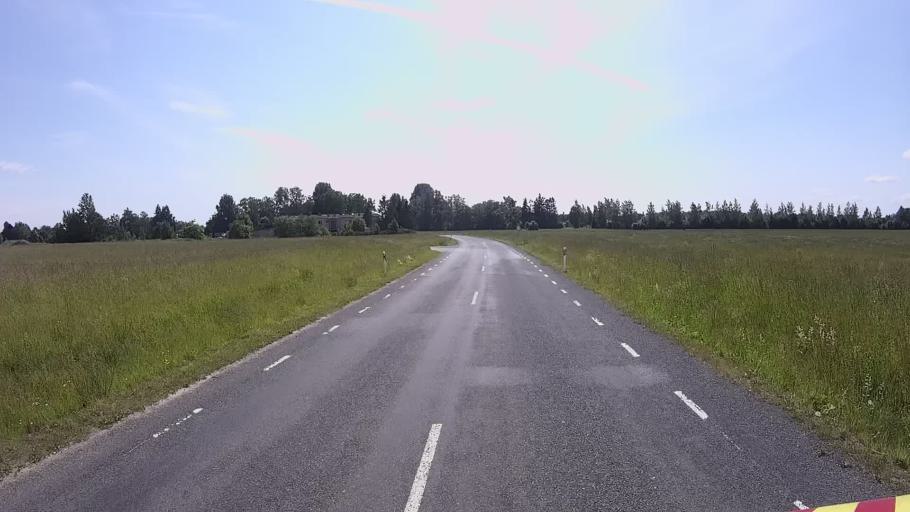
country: EE
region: Viljandimaa
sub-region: Karksi vald
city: Karksi-Nuia
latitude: 58.0672
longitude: 25.5519
